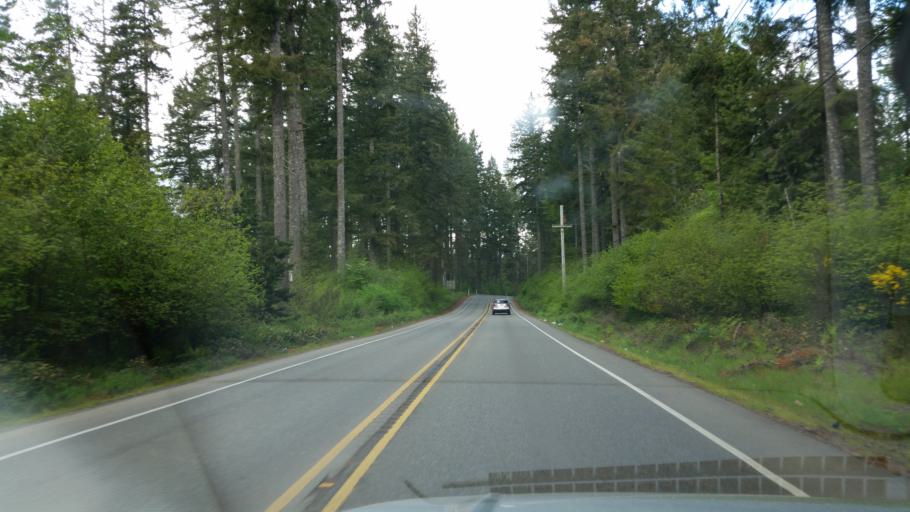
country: US
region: Washington
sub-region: Mason County
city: Allyn
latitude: 47.4110
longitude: -122.8417
